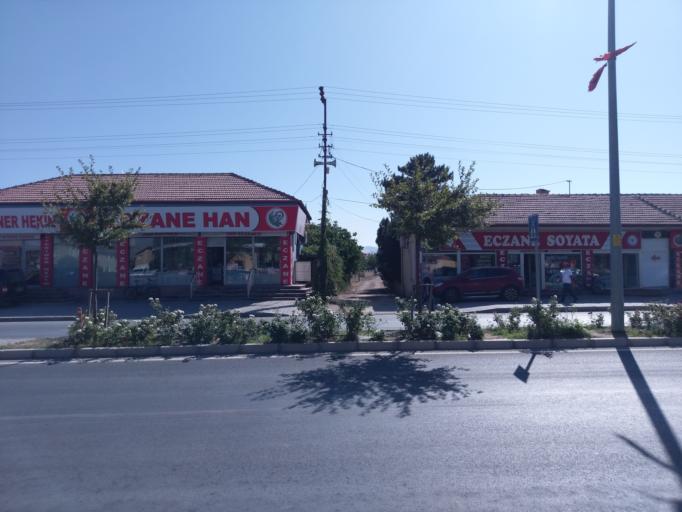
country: TR
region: Kayseri
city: Tomarza
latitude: 38.4535
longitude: 35.7996
